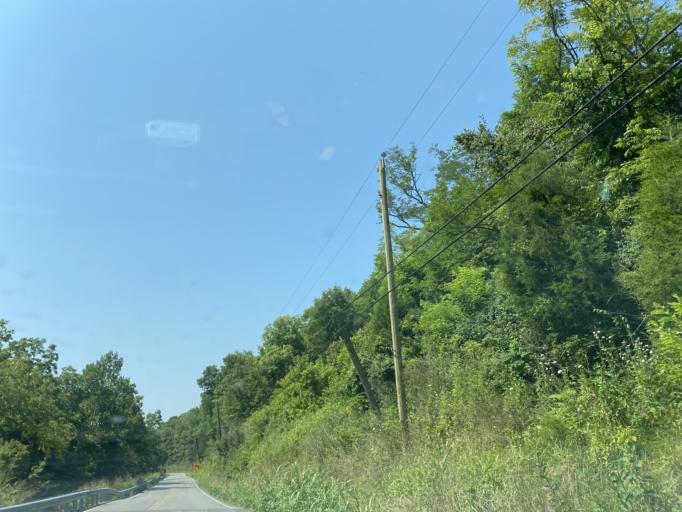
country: US
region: Kentucky
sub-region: Campbell County
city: Claryville
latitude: 38.8505
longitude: -84.4674
